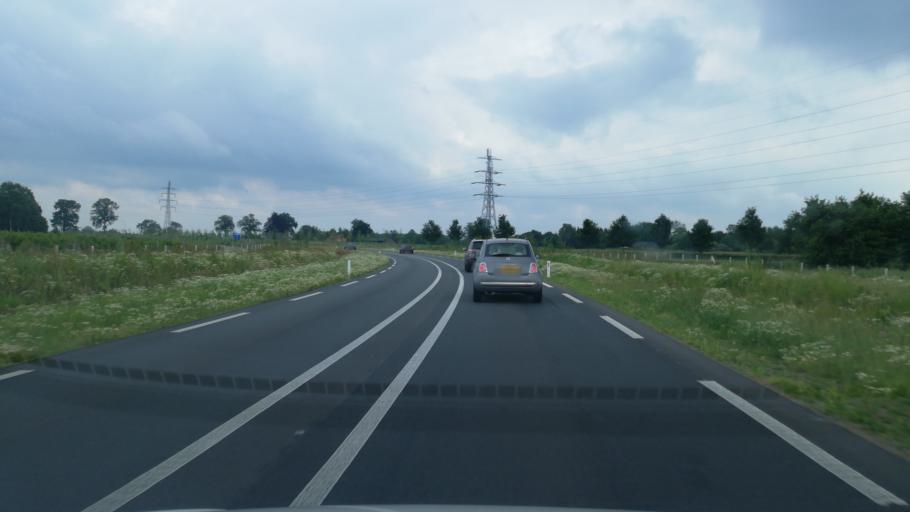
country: NL
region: Gelderland
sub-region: Gemeente Voorst
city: Voorst
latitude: 52.1624
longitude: 6.1370
